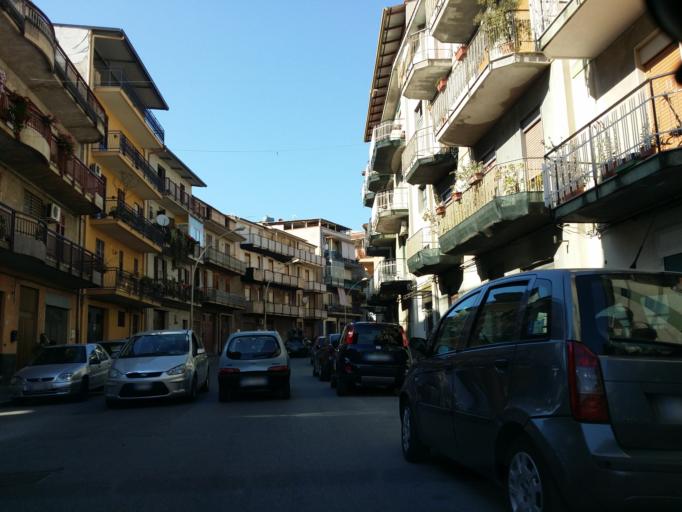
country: IT
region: Sicily
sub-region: Palermo
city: Misilmeri
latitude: 38.0345
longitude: 13.4552
